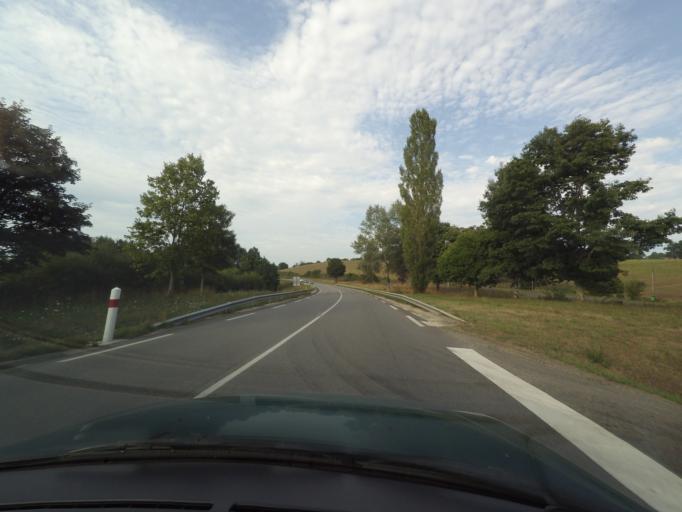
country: FR
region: Limousin
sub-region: Departement de la Haute-Vienne
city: Aixe-sur-Vienne
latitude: 45.7846
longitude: 1.1105
